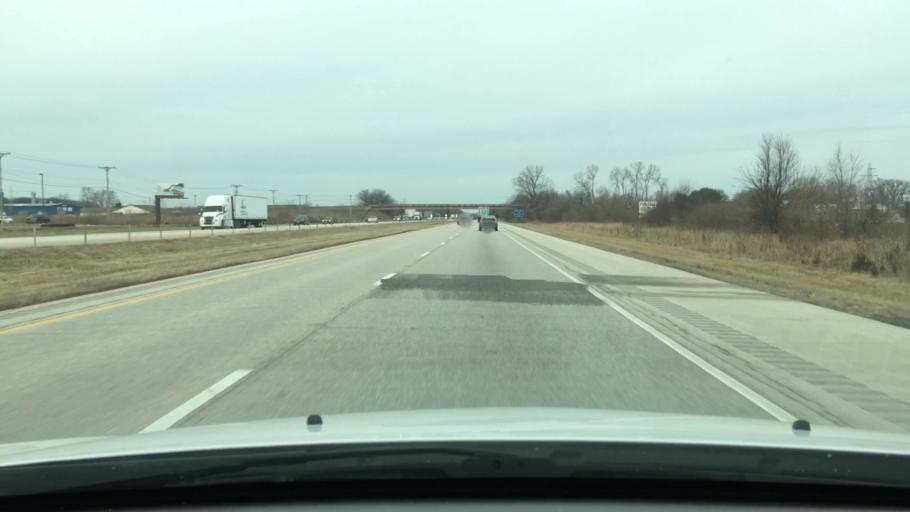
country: US
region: Illinois
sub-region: Sangamon County
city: Grandview
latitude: 39.8423
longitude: -89.5938
